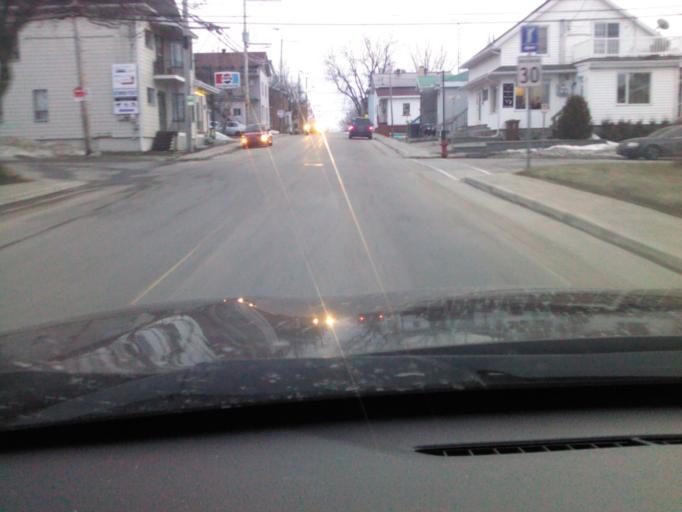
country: CA
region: Quebec
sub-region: Capitale-Nationale
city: Donnacona
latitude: 46.6758
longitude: -71.7368
